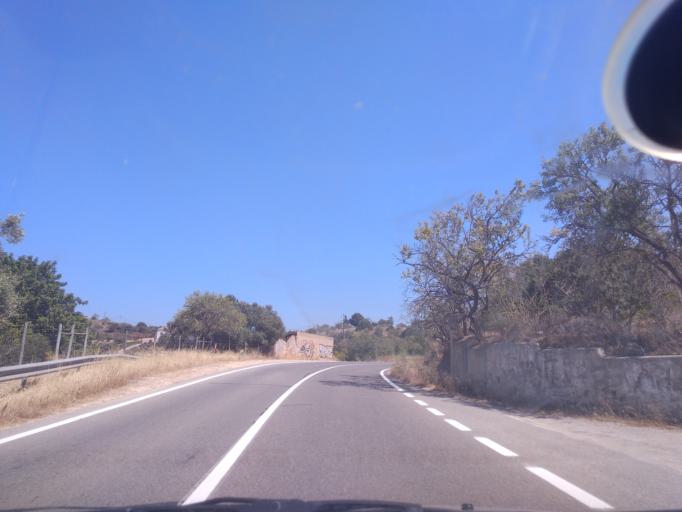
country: PT
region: Faro
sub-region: Lagos
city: Lagos
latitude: 37.1192
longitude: -8.6922
